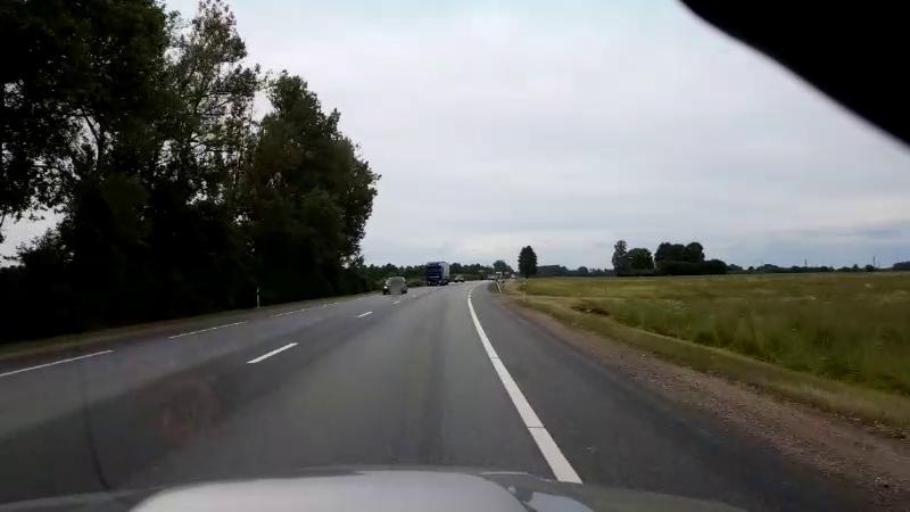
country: LV
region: Lecava
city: Iecava
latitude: 56.5858
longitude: 24.1856
